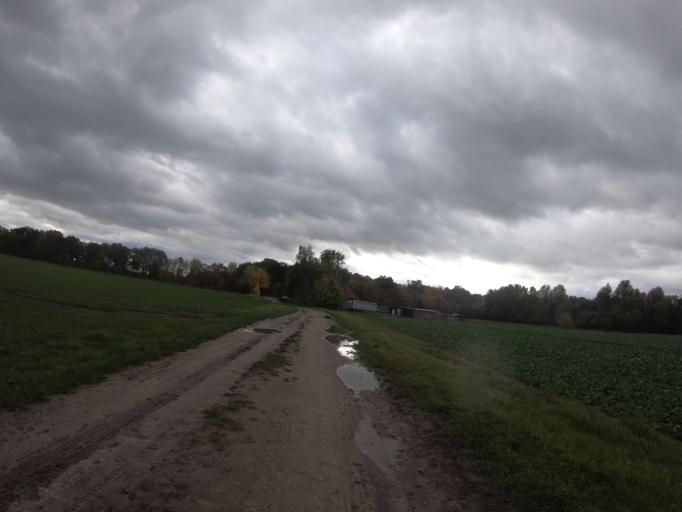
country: DE
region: Lower Saxony
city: Adenbuettel
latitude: 52.3958
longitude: 10.4819
